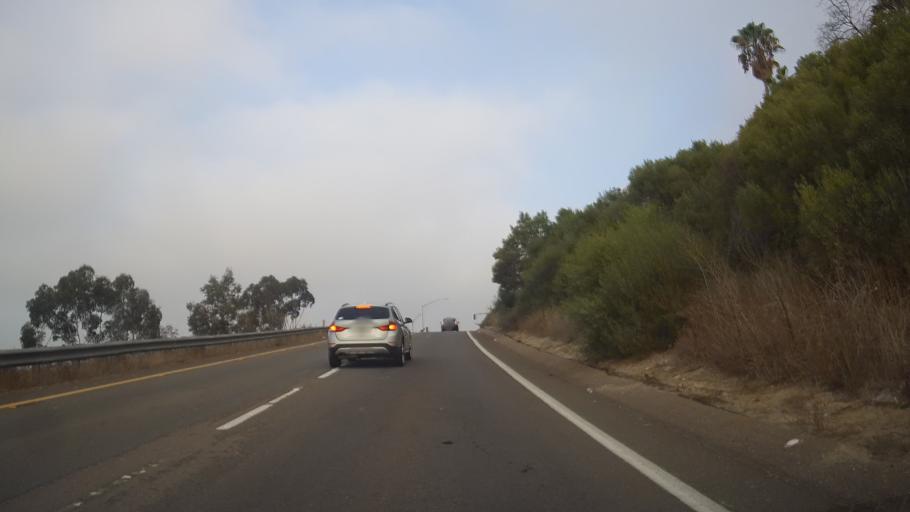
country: US
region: California
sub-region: San Diego County
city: San Diego
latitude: 32.7852
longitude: -117.1436
